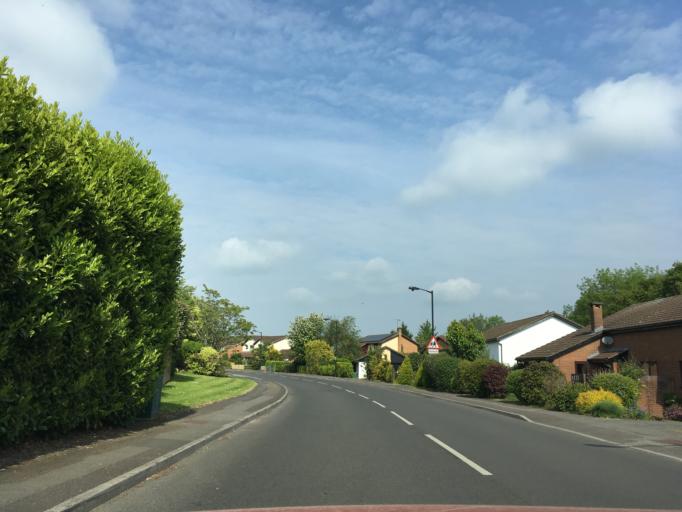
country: GB
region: England
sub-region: North Somerset
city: Nailsea
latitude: 51.4254
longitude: -2.7649
